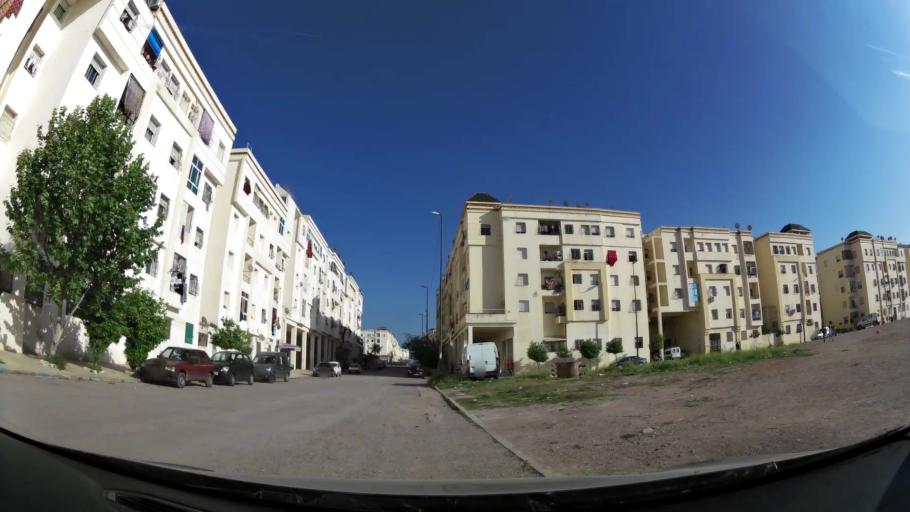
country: MA
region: Fes-Boulemane
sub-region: Fes
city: Fes
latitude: 34.0164
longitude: -5.0422
